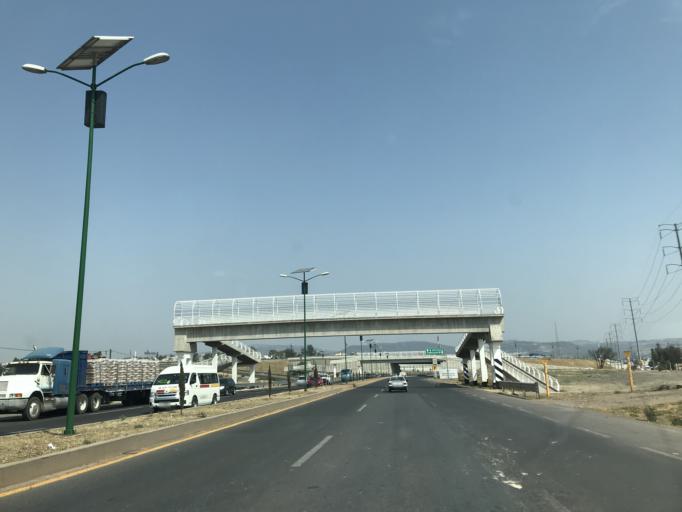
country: MX
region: Tlaxcala
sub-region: Chiautempan
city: Santa Cruz Tetela
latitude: 19.3016
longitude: -98.1973
